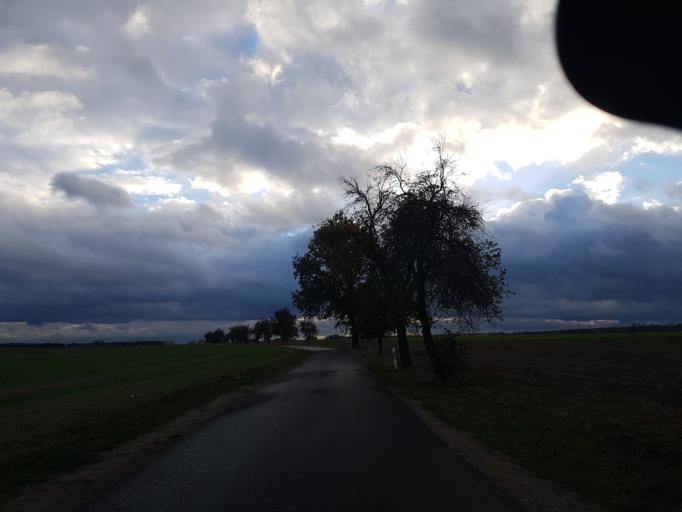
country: DE
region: Saxony-Anhalt
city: Seyda
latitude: 51.9015
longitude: 12.9055
